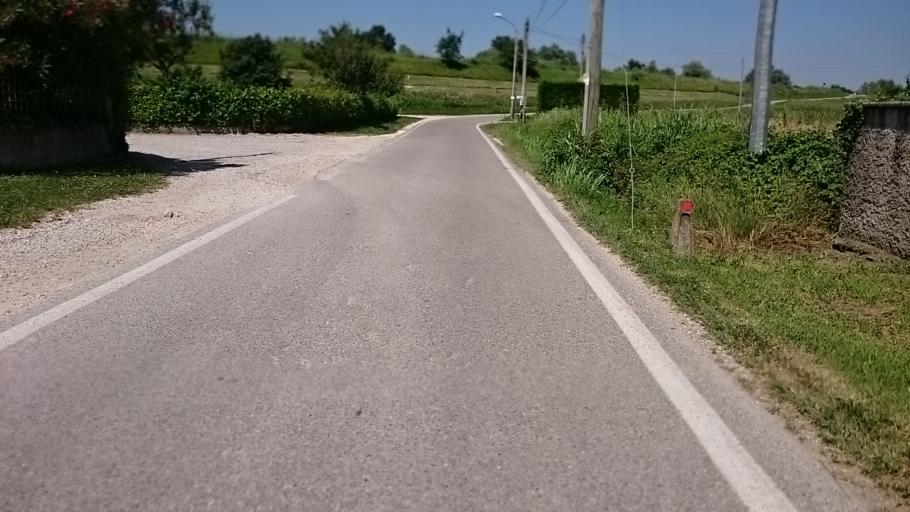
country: IT
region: Veneto
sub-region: Provincia di Venezia
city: Galta
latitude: 45.3720
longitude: 12.0305
